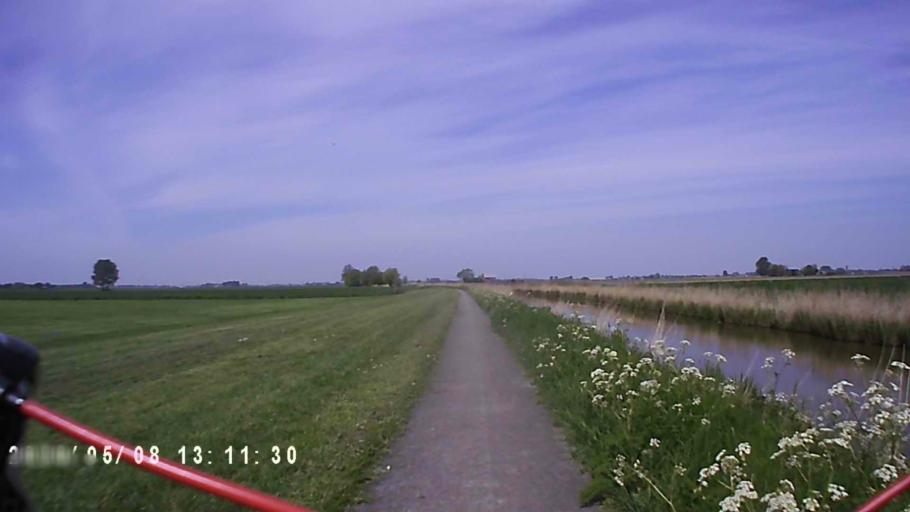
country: NL
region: Groningen
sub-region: Gemeente Bedum
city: Bedum
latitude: 53.2952
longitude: 6.6923
